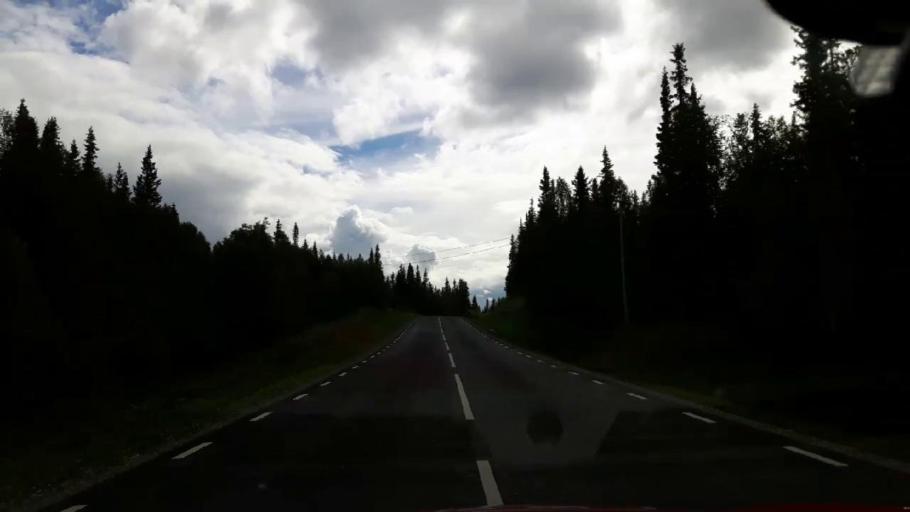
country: NO
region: Nord-Trondelag
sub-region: Royrvik
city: Royrvik
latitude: 64.8138
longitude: 14.0641
